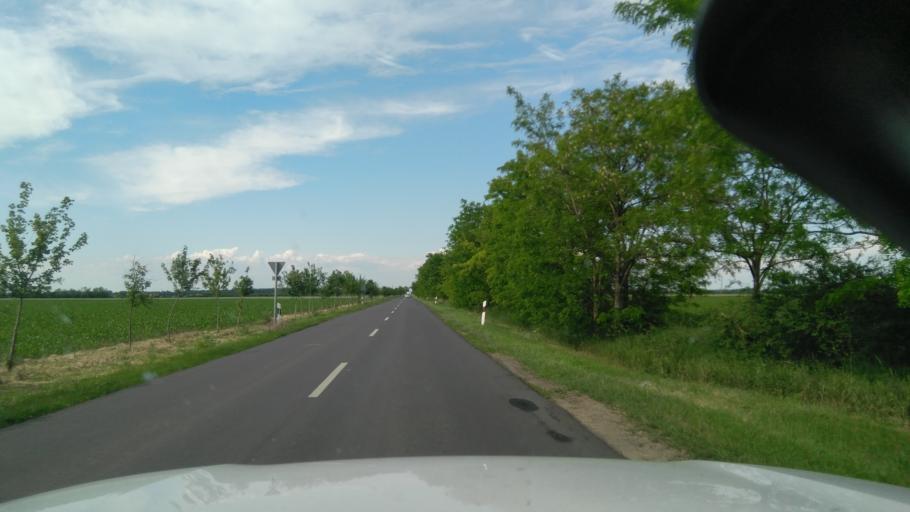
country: HU
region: Bekes
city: Medgyesegyhaza
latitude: 46.5152
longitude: 20.9747
